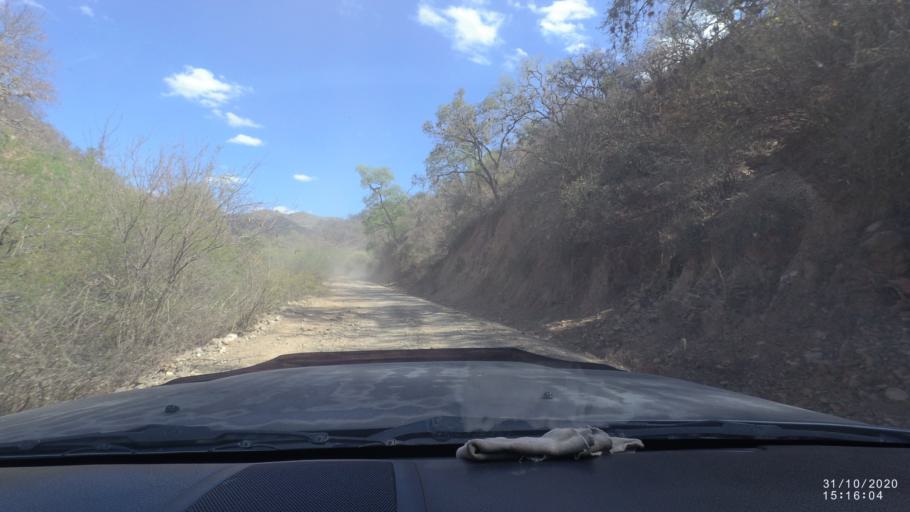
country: BO
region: Cochabamba
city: Aiquile
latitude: -18.3331
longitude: -64.7736
